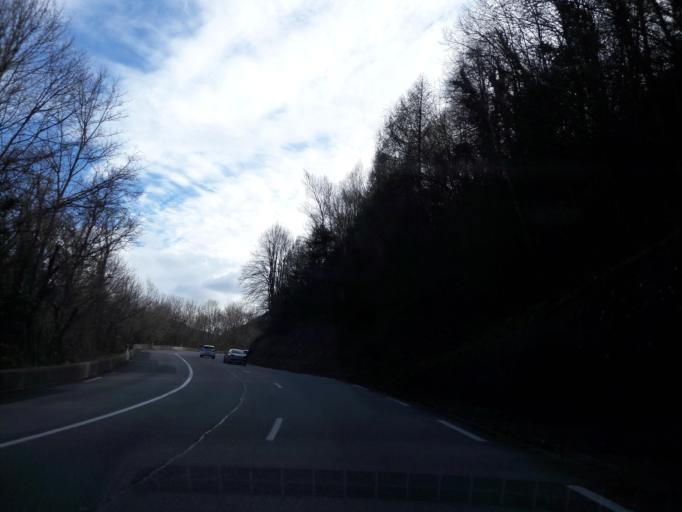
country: FR
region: Rhone-Alpes
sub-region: Departement de l'Isere
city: Notre-Dame-de-Mesage
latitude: 45.0553
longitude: 5.7525
